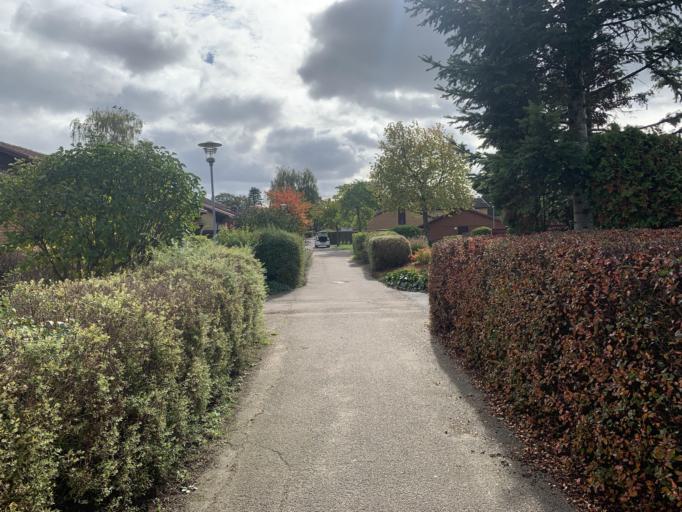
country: SE
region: Skane
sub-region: Kristianstads Kommun
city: Kristianstad
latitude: 56.0303
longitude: 14.2045
